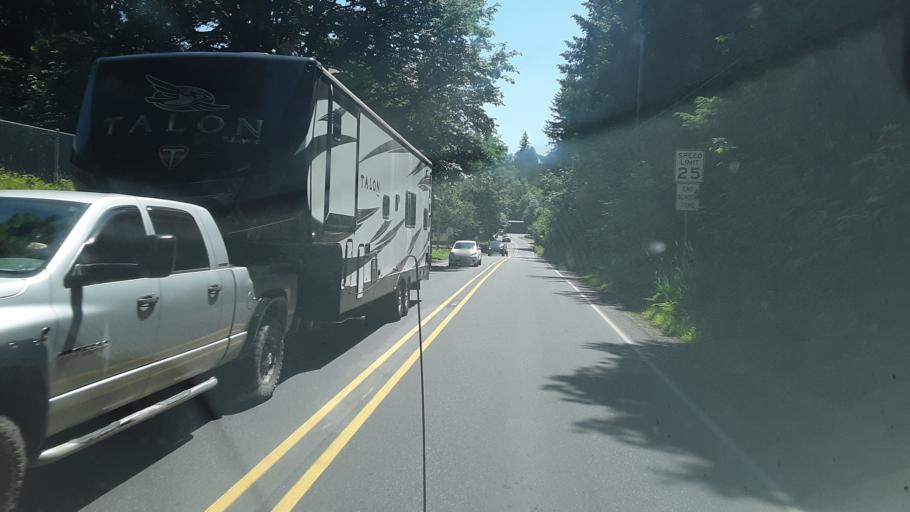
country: US
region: Washington
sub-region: Clark County
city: Amboy
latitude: 45.9128
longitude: -122.4468
